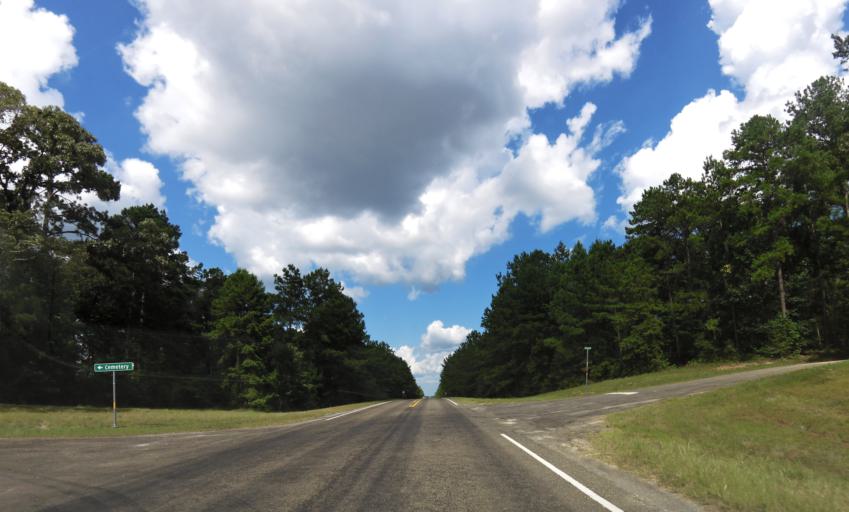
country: US
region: Texas
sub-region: Newton County
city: Newton
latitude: 31.1032
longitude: -93.7017
